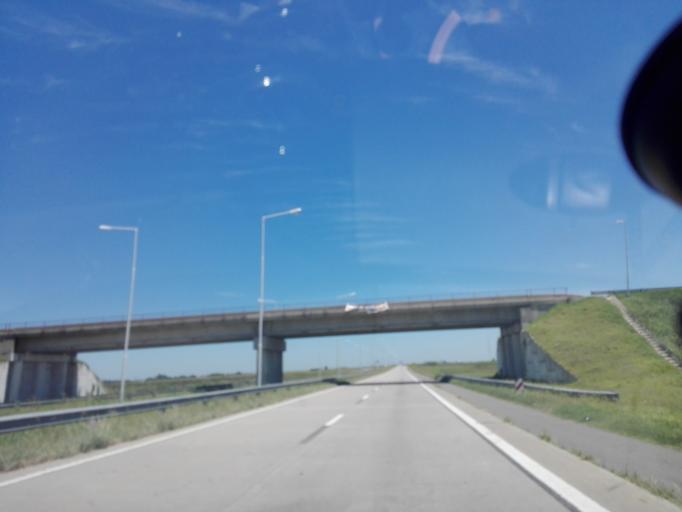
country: AR
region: Cordoba
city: Marcos Juarez
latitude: -32.6689
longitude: -62.0699
